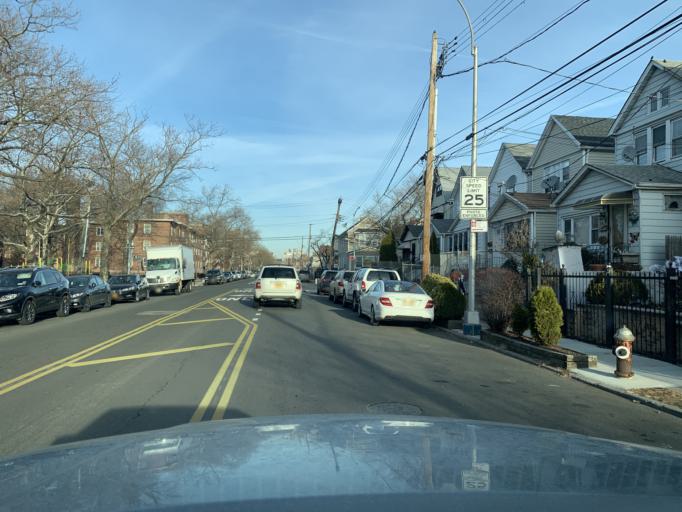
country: US
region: New York
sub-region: Queens County
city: Jamaica
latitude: 40.6953
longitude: -73.7929
